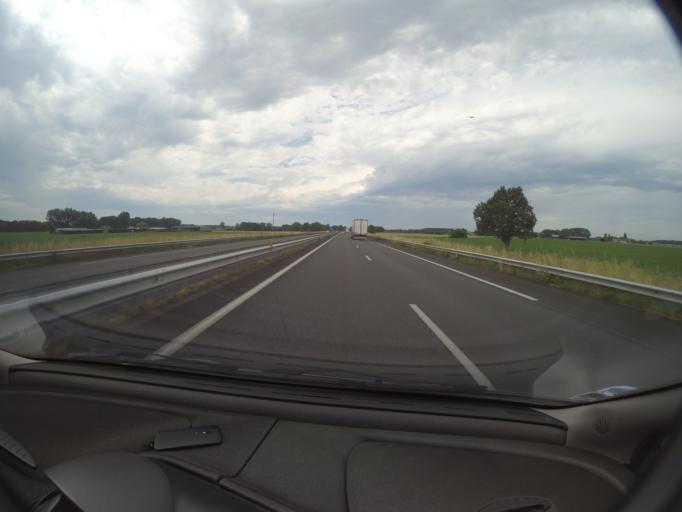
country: FR
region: Pays de la Loire
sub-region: Departement de Maine-et-Loire
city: Le Plessis-Grammoire
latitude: 47.5173
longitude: -0.3949
